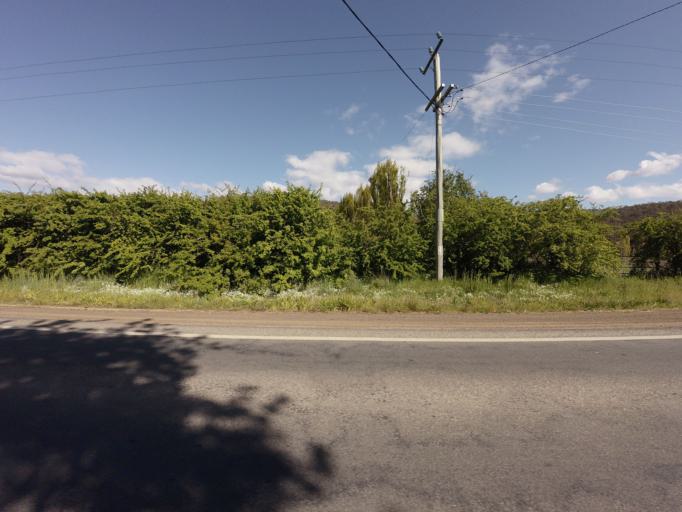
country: AU
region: Tasmania
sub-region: Derwent Valley
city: New Norfolk
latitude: -42.7780
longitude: 147.0479
